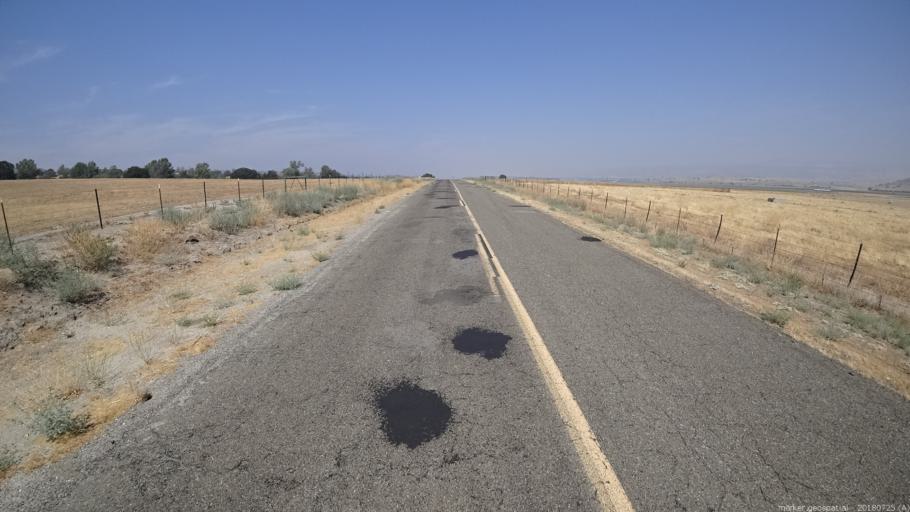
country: US
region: California
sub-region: San Luis Obispo County
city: Shandon
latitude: 35.8071
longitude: -120.3694
